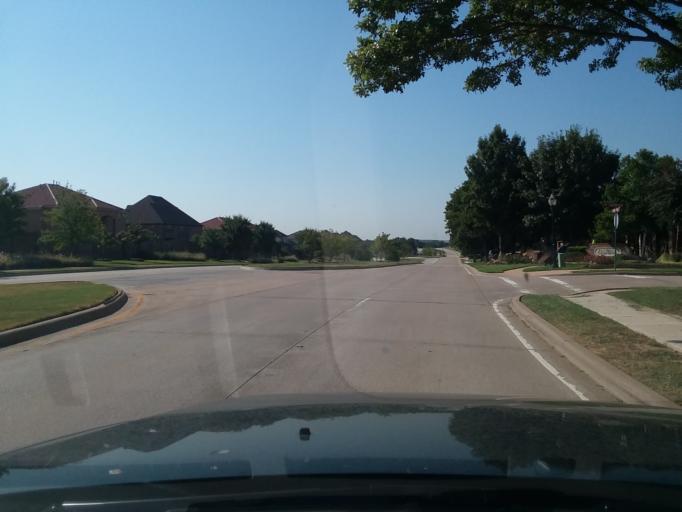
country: US
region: Texas
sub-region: Denton County
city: Lewisville
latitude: 33.0086
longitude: -97.0366
